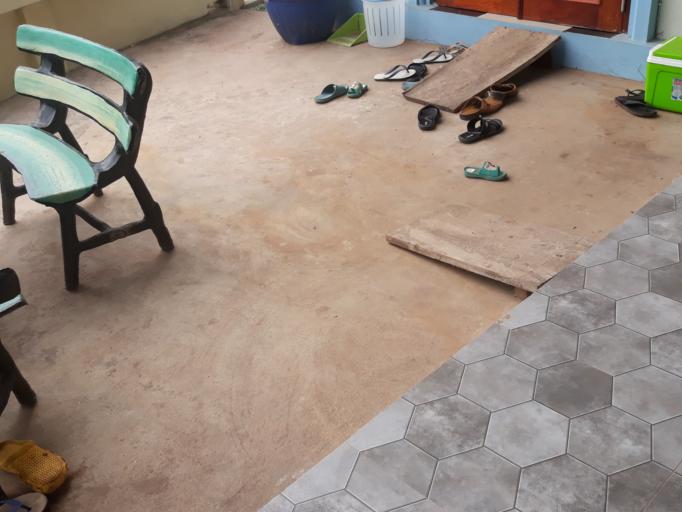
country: LA
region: Xiagnabouli
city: Sainyabuli
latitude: 19.2581
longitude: 101.7065
